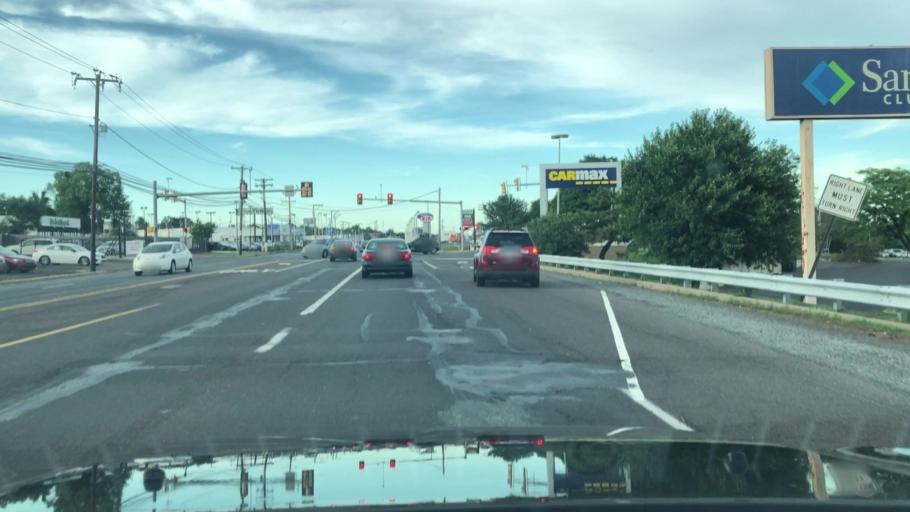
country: US
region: Pennsylvania
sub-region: Bucks County
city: Woodbourne
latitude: 40.1737
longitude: -74.8889
